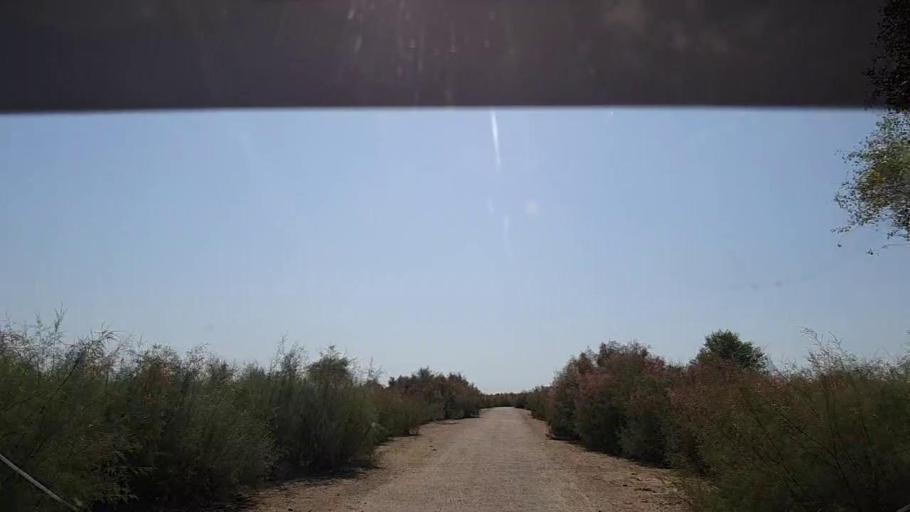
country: PK
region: Sindh
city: Ghauspur
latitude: 28.2042
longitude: 69.0763
